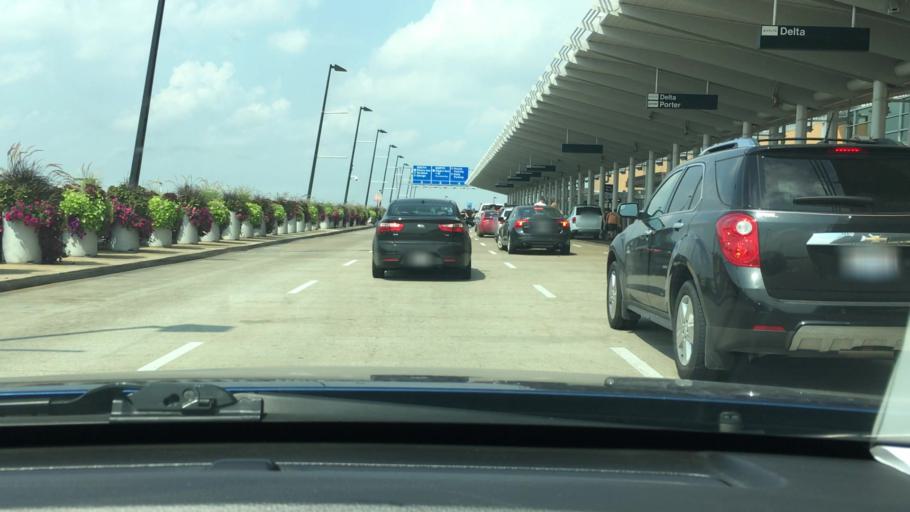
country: US
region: Illinois
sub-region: Cook County
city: Stickney
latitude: 41.7880
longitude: -87.7410
